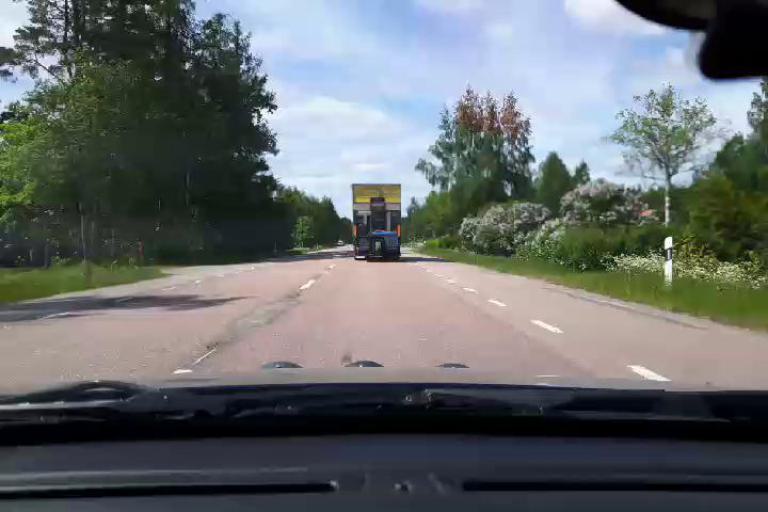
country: SE
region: Uppsala
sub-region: Osthammars Kommun
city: Bjorklinge
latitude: 60.1097
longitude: 17.5357
